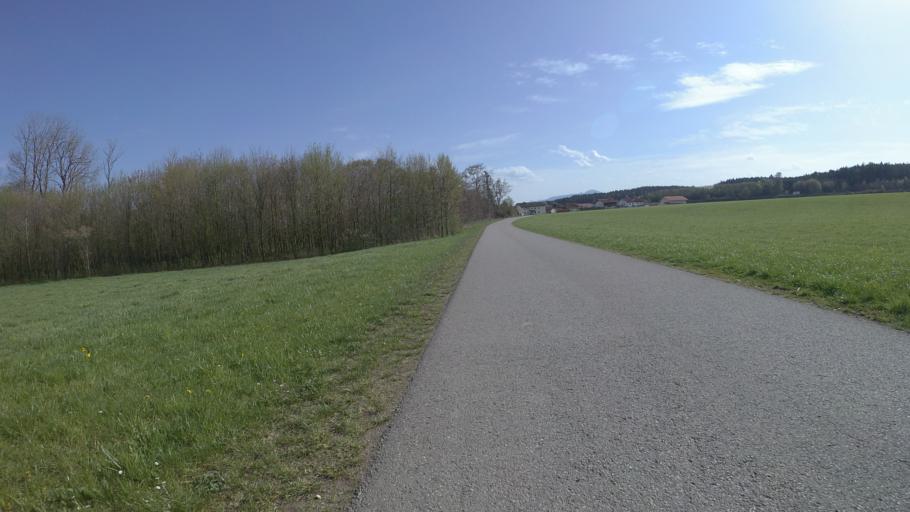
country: DE
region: Bavaria
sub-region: Upper Bavaria
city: Nussdorf
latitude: 47.9134
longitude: 12.6160
